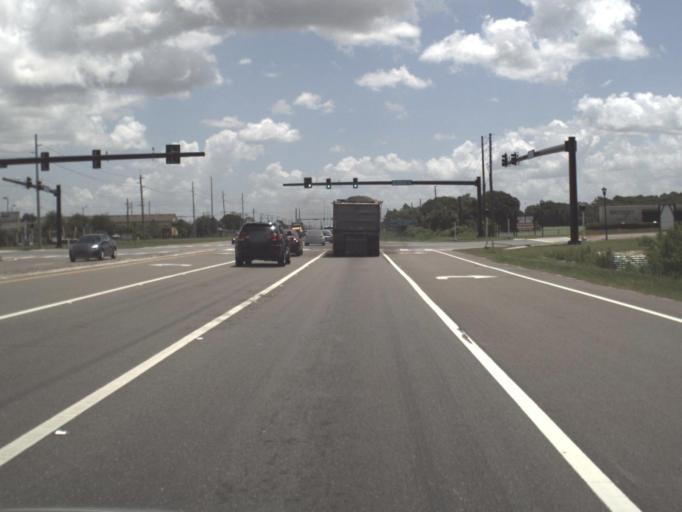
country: US
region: Florida
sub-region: Hillsborough County
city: Apollo Beach
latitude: 27.7921
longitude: -82.3729
